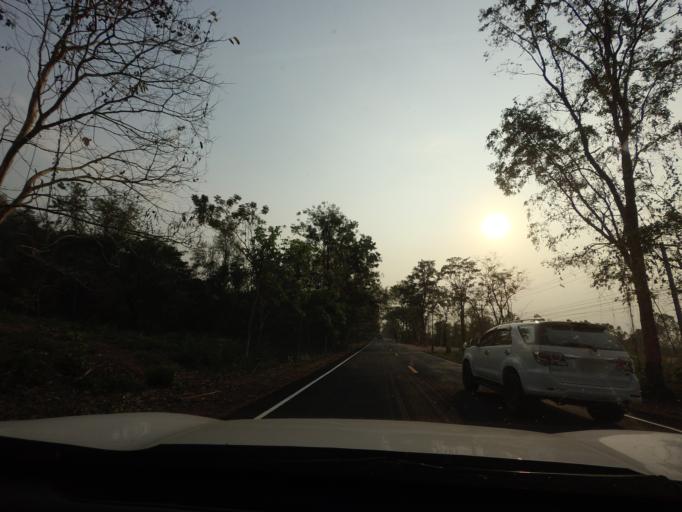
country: TH
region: Nakhon Nayok
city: Pak Phli
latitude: 14.1897
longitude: 101.3783
